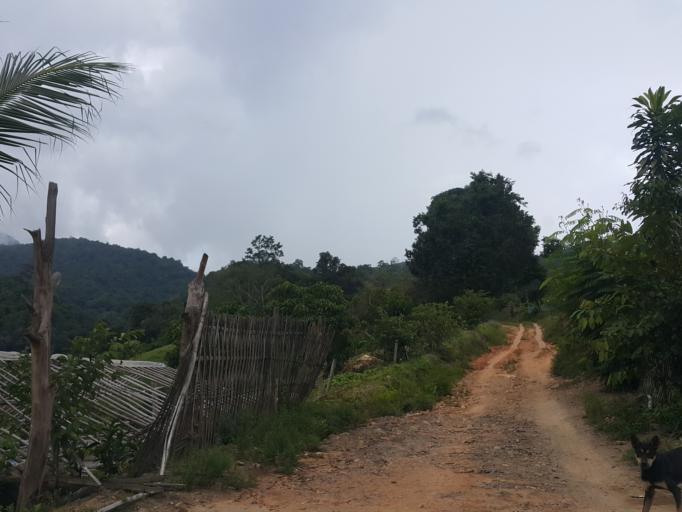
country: TH
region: Chiang Mai
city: Phrao
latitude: 19.3193
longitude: 99.1172
